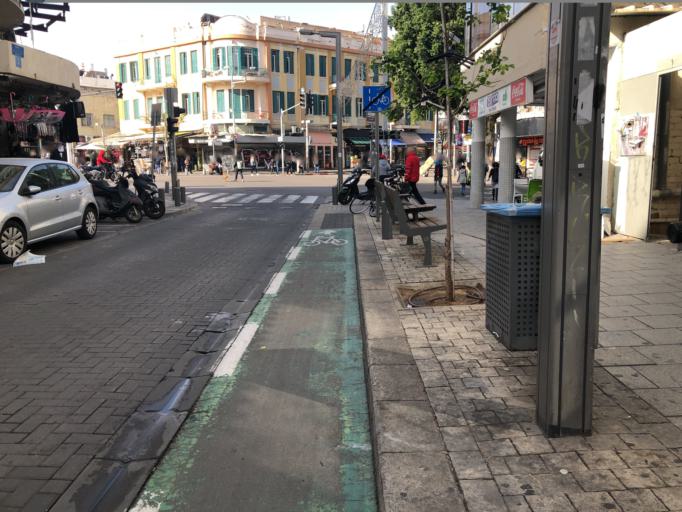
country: IL
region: Tel Aviv
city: Tel Aviv
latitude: 32.0697
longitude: 34.7709
